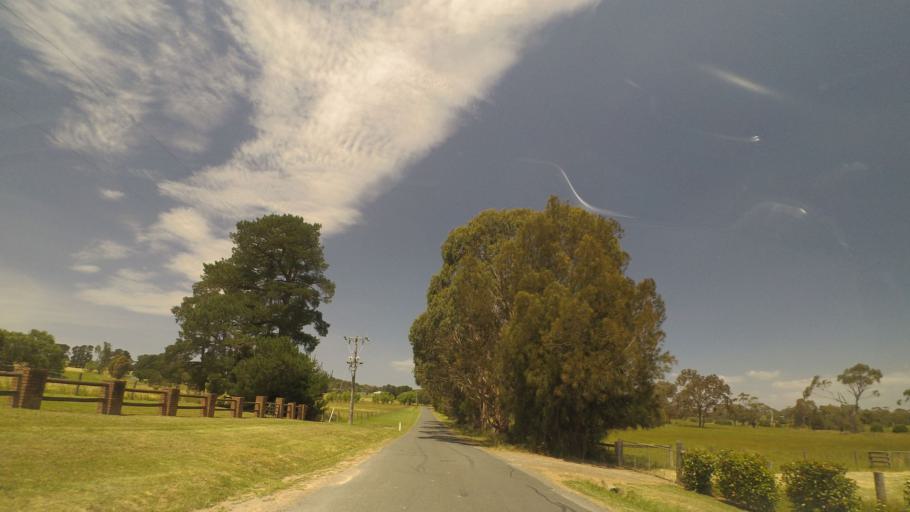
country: AU
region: Victoria
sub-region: Yarra Ranges
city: Chirnside Park
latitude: -37.7473
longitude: 145.2936
